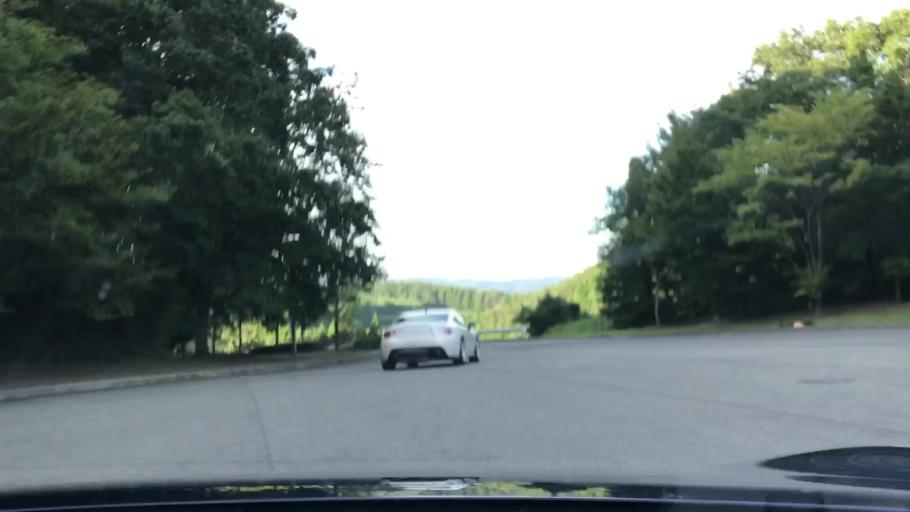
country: JP
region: Tochigi
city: Motegi
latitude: 36.5419
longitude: 140.2304
